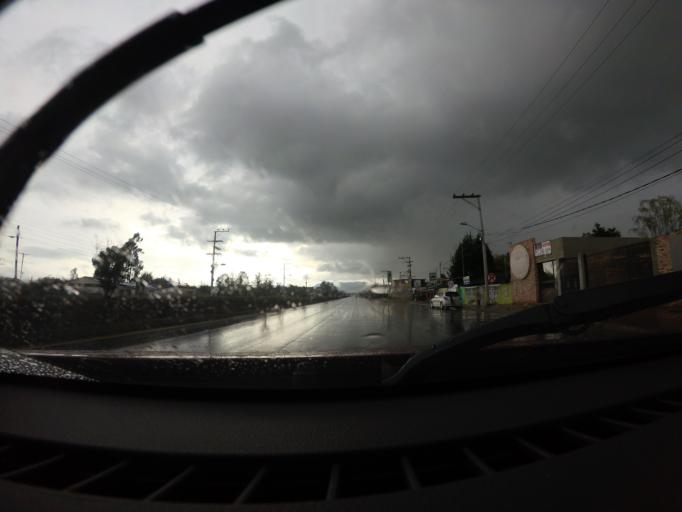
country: CO
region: Cundinamarca
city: El Rosal
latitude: 4.8164
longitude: -74.2247
